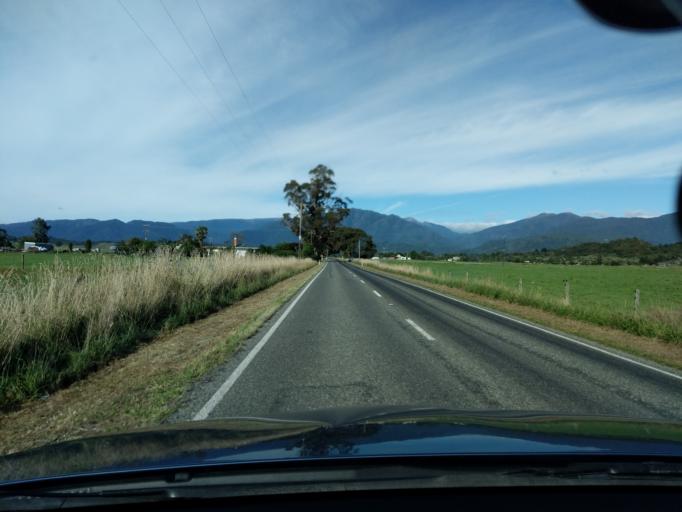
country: NZ
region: Tasman
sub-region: Tasman District
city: Takaka
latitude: -40.8478
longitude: 172.8354
